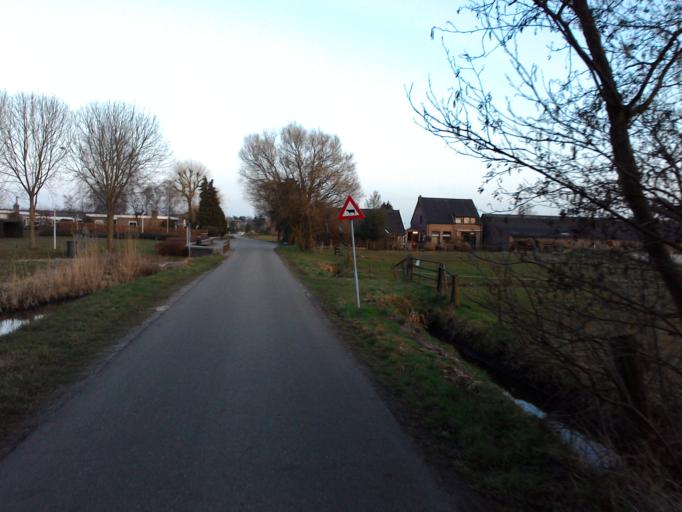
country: NL
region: Utrecht
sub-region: Gemeente Utrecht
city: Utrecht
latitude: 52.1278
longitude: 5.1348
